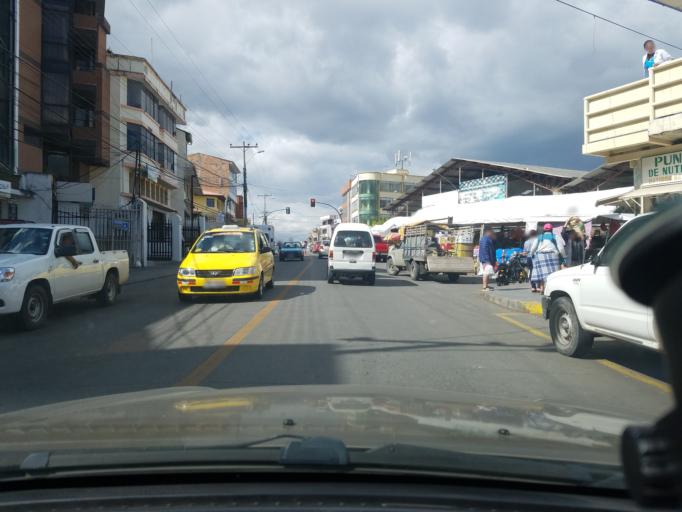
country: EC
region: Azuay
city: Cuenca
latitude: -2.9025
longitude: -78.9929
